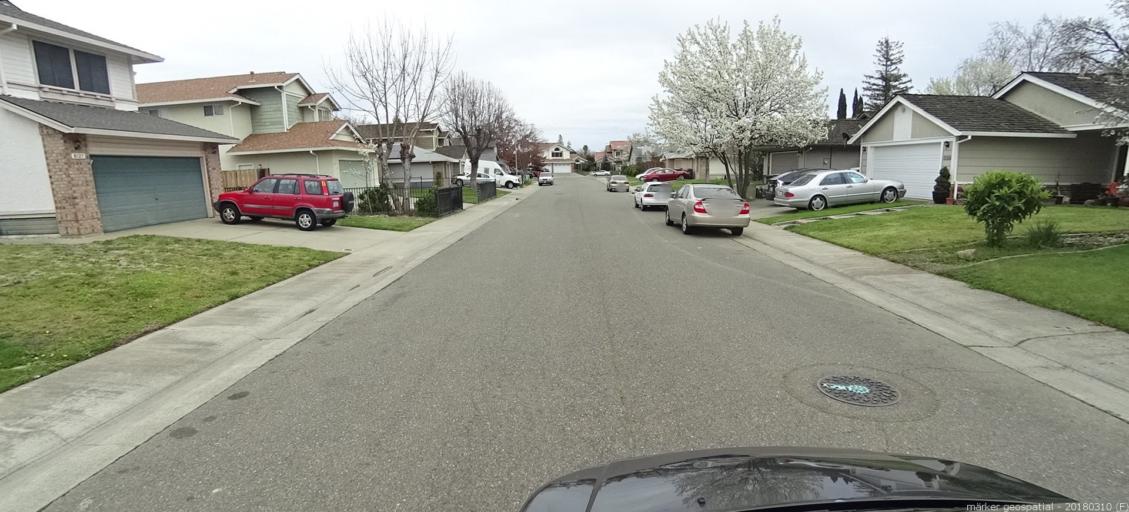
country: US
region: California
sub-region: Sacramento County
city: Vineyard
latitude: 38.4580
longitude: -121.3765
